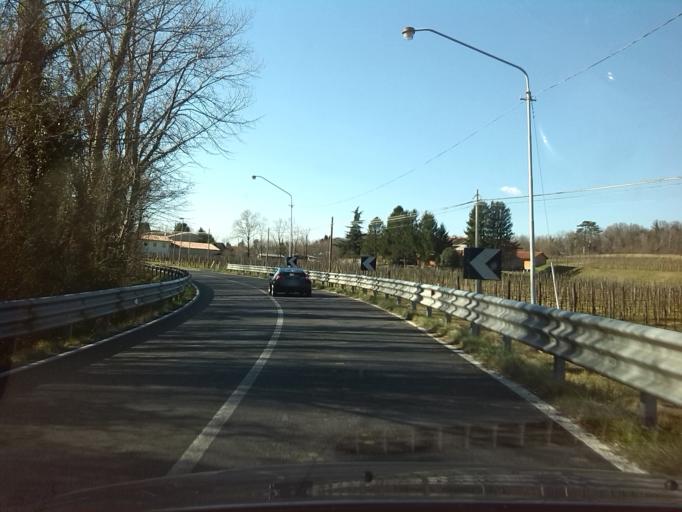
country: IT
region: Friuli Venezia Giulia
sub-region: Provincia di Udine
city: Moimacco
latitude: 46.1258
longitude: 13.3747
